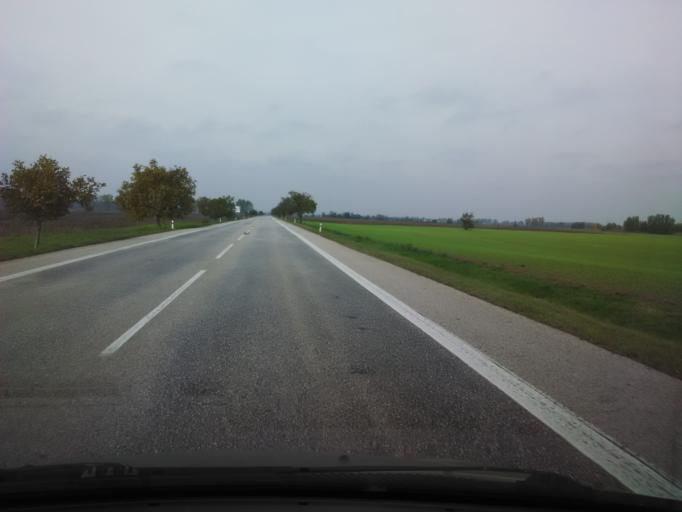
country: SK
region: Nitriansky
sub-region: Okres Komarno
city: Hurbanovo
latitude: 47.8214
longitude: 18.1782
